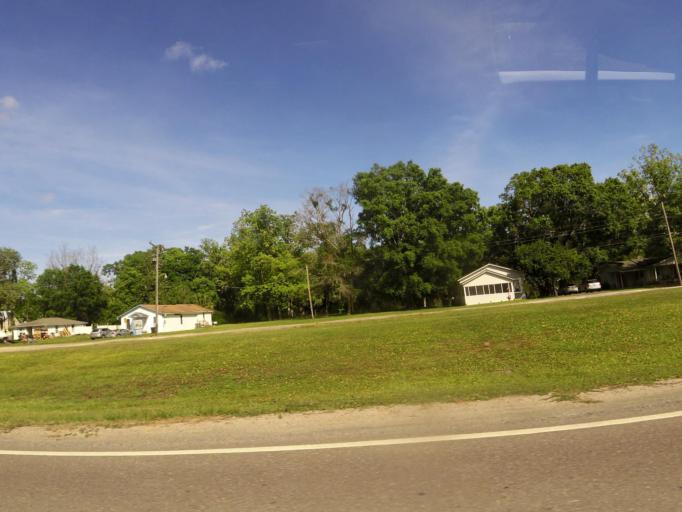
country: US
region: Florida
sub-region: Nassau County
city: Callahan
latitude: 30.5631
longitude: -81.8346
